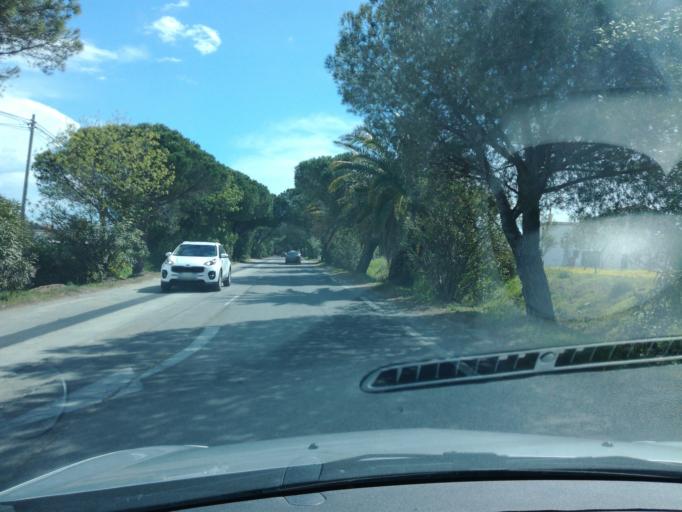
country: FR
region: Provence-Alpes-Cote d'Azur
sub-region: Departement du Var
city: Hyeres
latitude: 43.1159
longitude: 6.1484
